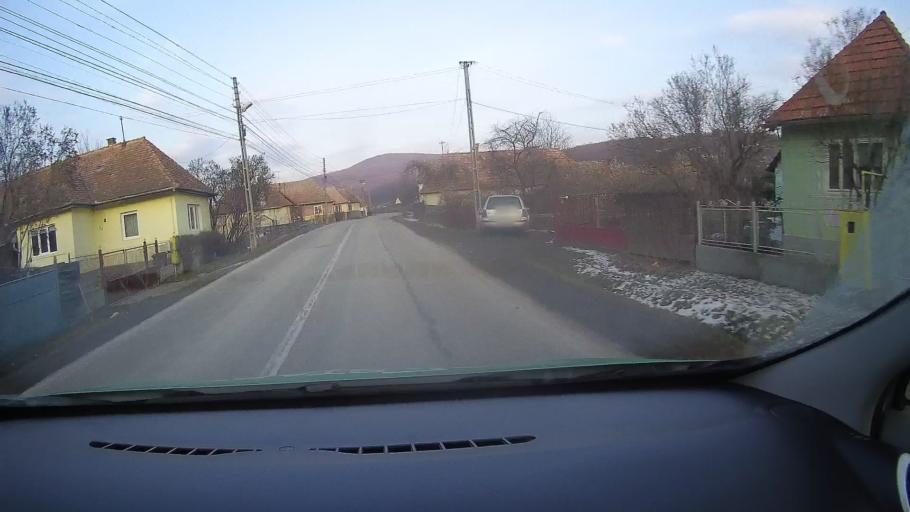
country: RO
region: Harghita
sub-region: Oras Cristuru Secuiesc
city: Cristuru Secuiesc
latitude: 46.3007
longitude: 25.0670
